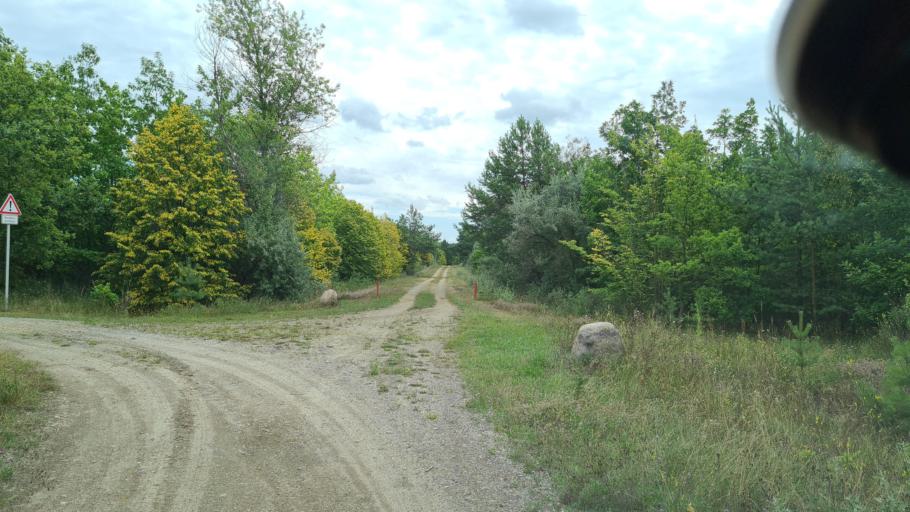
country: DE
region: Brandenburg
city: Spremberg
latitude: 51.5814
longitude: 14.3103
